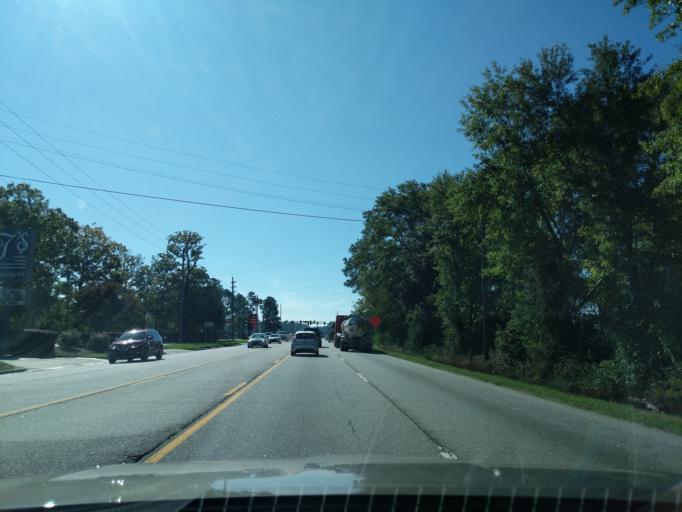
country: US
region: Georgia
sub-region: Richmond County
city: Augusta
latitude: 33.3965
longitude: -82.0055
